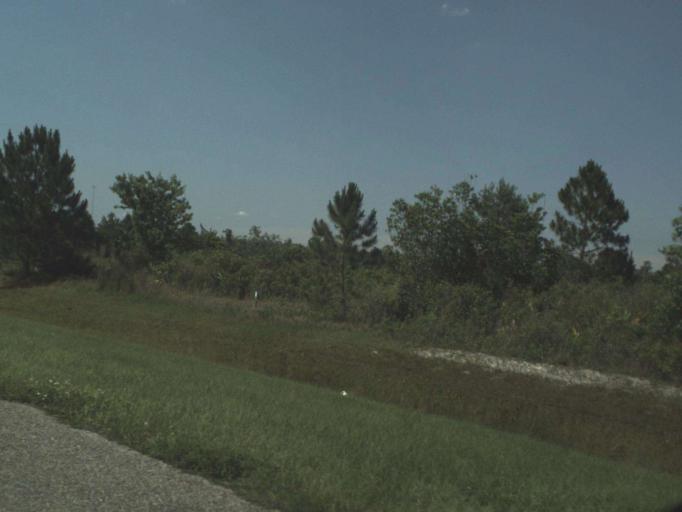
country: US
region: Florida
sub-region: Orange County
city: Wedgefield
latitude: 28.5222
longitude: -81.0689
